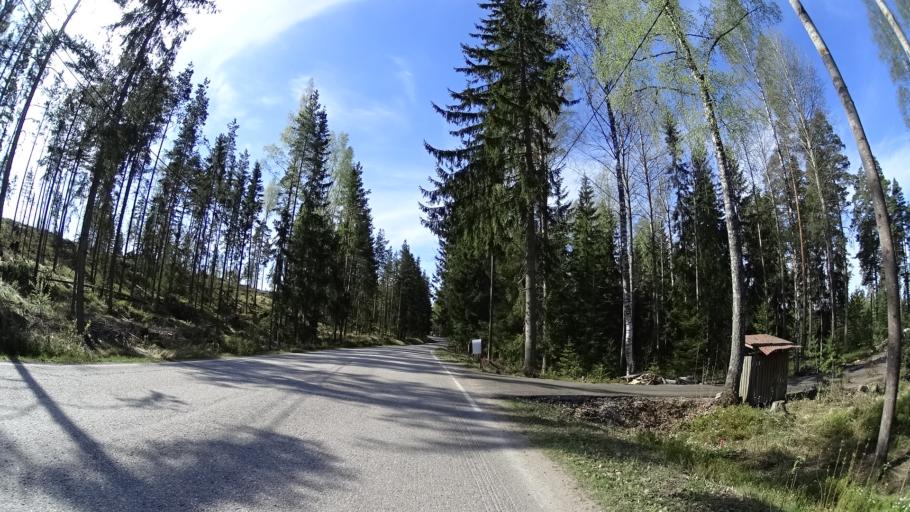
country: FI
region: Uusimaa
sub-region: Helsinki
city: Nurmijaervi
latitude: 60.4507
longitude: 24.8254
